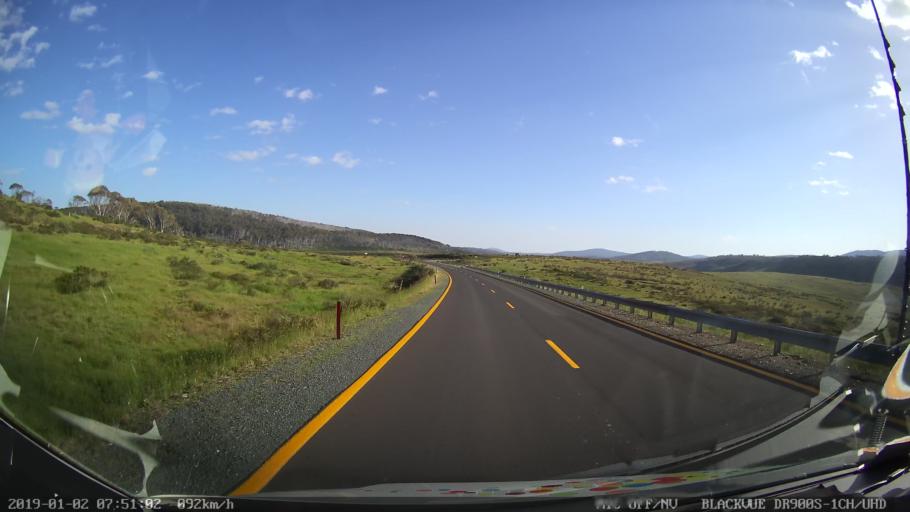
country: AU
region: New South Wales
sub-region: Tumut Shire
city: Tumut
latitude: -35.7232
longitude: 148.5306
